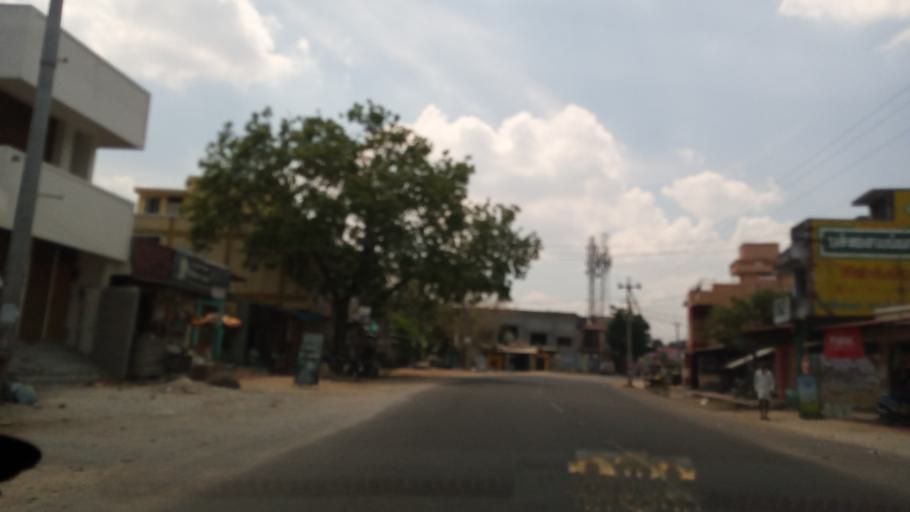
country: IN
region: Tamil Nadu
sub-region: Vellore
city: Walajapet
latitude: 12.9240
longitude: 79.3719
